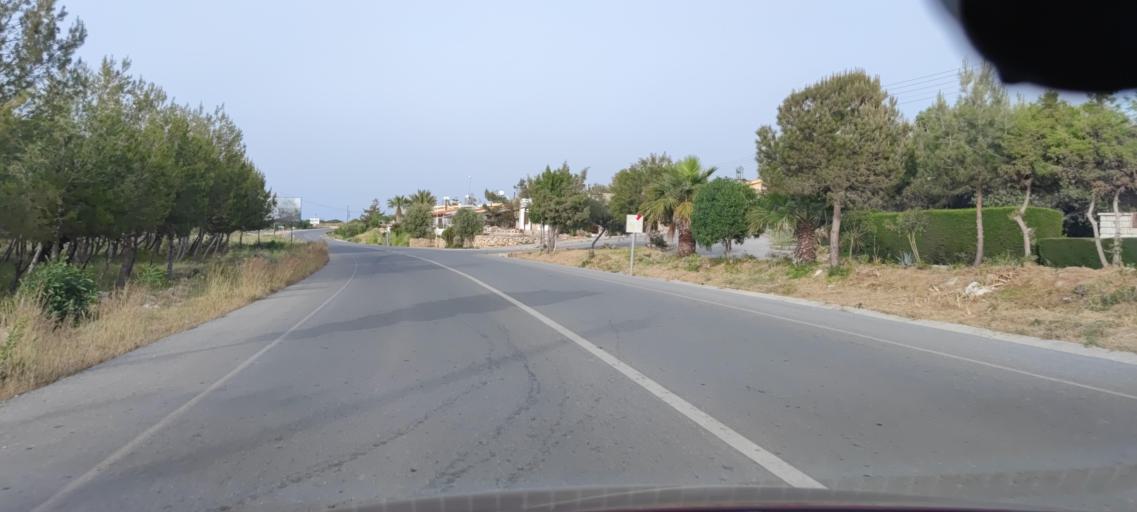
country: CY
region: Ammochostos
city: Leonarisso
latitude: 35.5541
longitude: 34.2159
